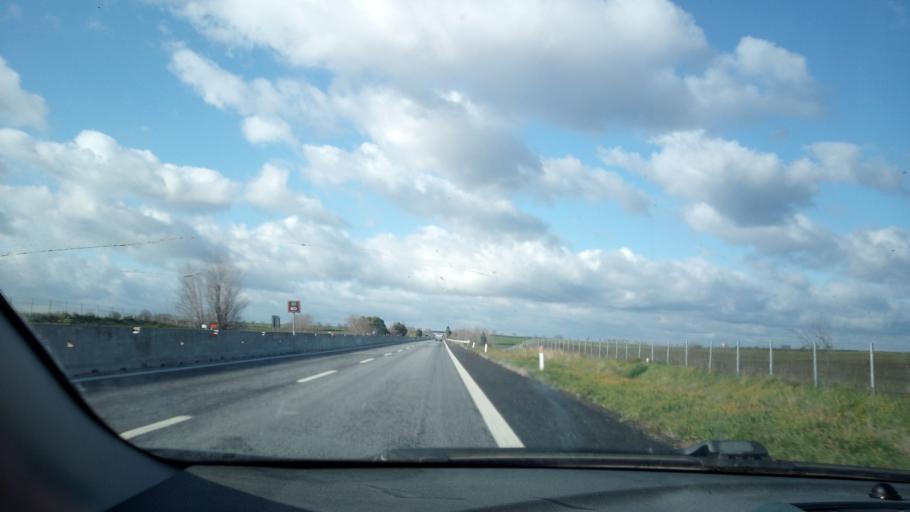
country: IT
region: Apulia
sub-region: Provincia di Foggia
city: Stornarella
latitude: 41.1790
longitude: 15.7337
